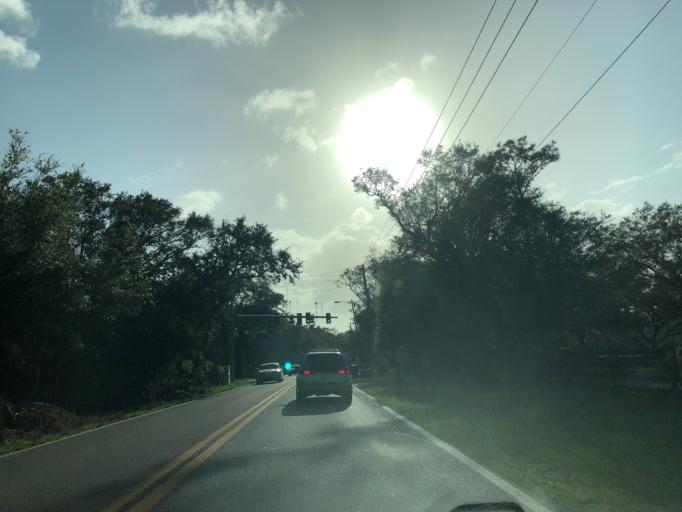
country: US
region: Florida
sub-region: Orange County
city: Alafaya
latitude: 28.5859
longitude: -81.1585
